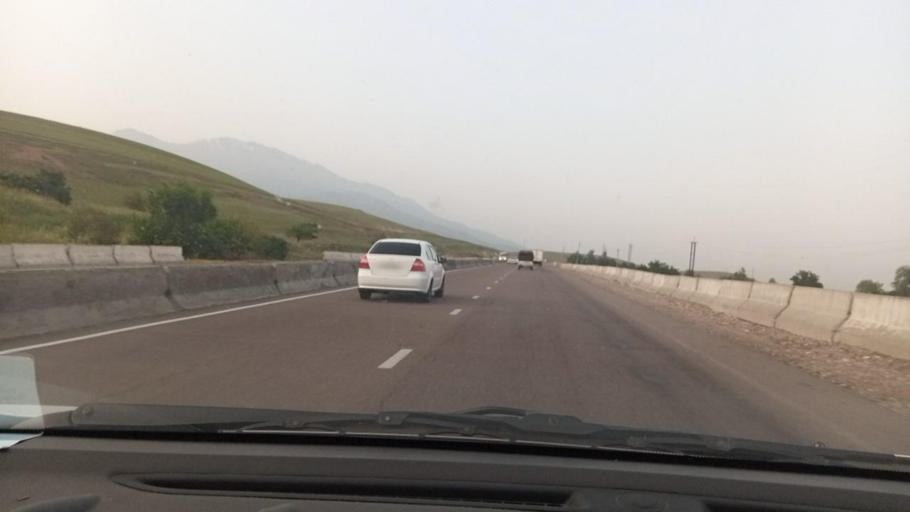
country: UZ
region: Toshkent
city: Angren
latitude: 41.0535
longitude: 70.1630
